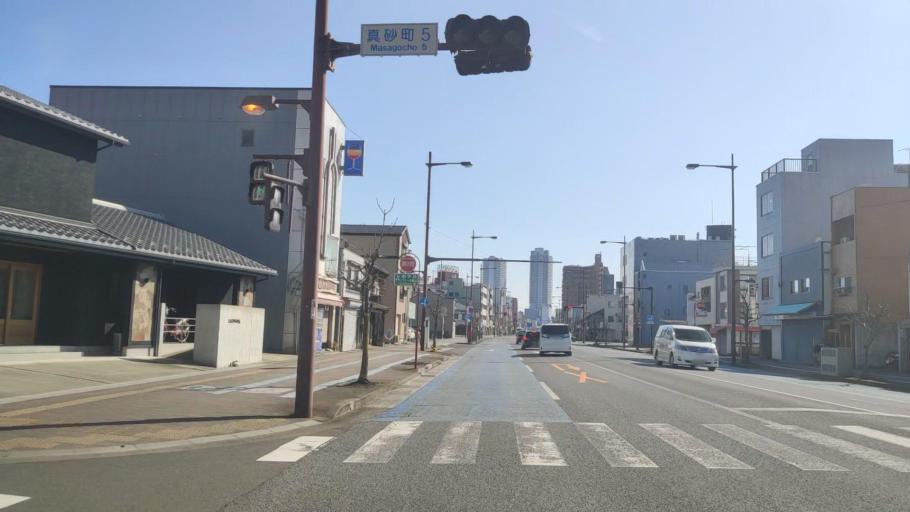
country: JP
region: Gifu
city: Gifu-shi
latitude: 35.4225
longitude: 136.7521
